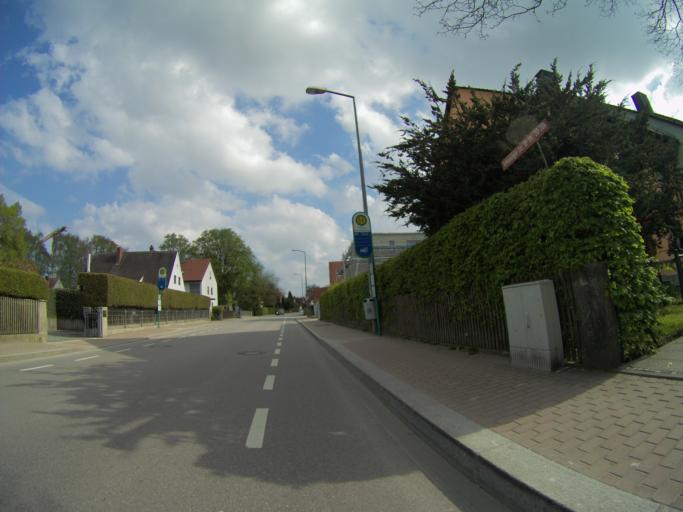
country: DE
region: Bavaria
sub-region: Upper Bavaria
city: Freising
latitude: 48.3944
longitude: 11.7527
